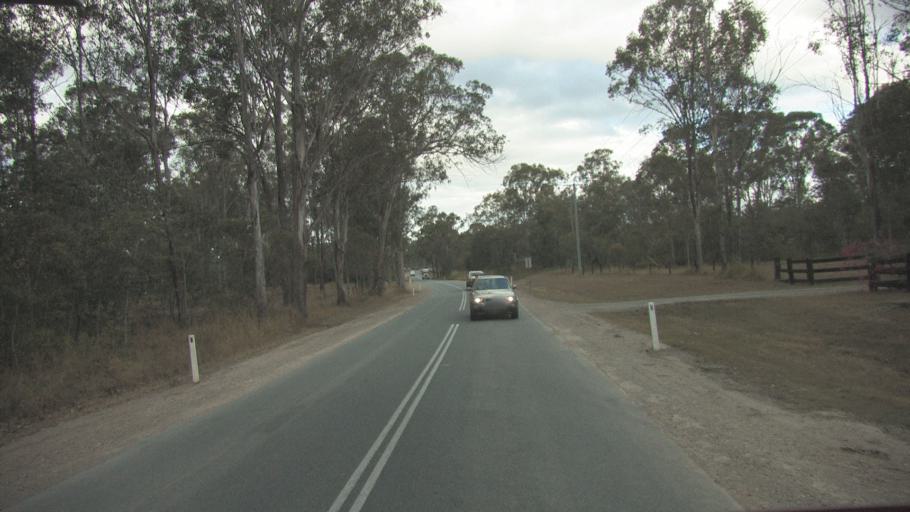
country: AU
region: Queensland
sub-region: Logan
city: Cedar Vale
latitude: -27.8477
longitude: 153.0506
